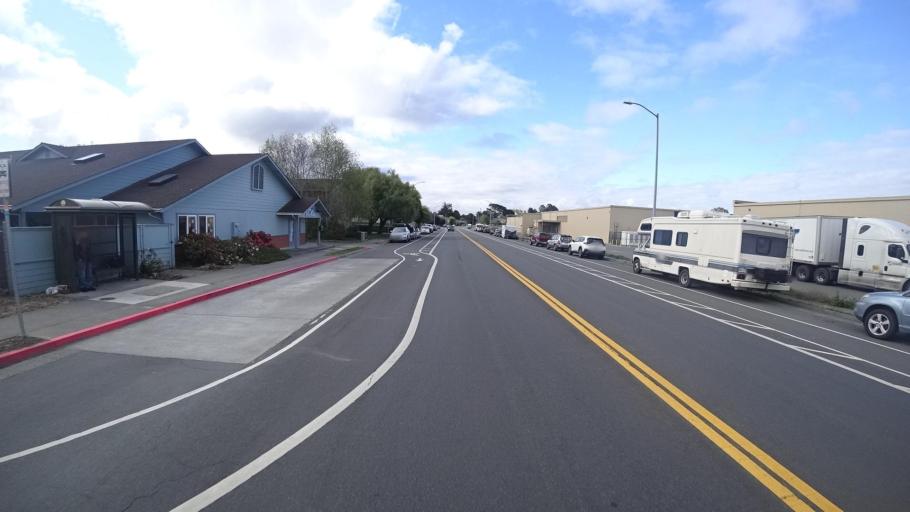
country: US
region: California
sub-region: Humboldt County
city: Arcata
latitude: 40.9040
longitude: -124.0812
